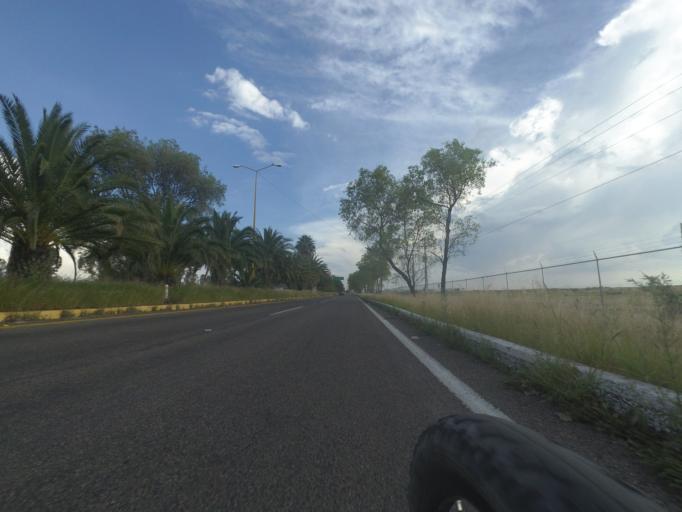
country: MX
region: Aguascalientes
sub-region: Aguascalientes
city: Penuelas (El Cienegal)
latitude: 21.7127
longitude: -102.3106
